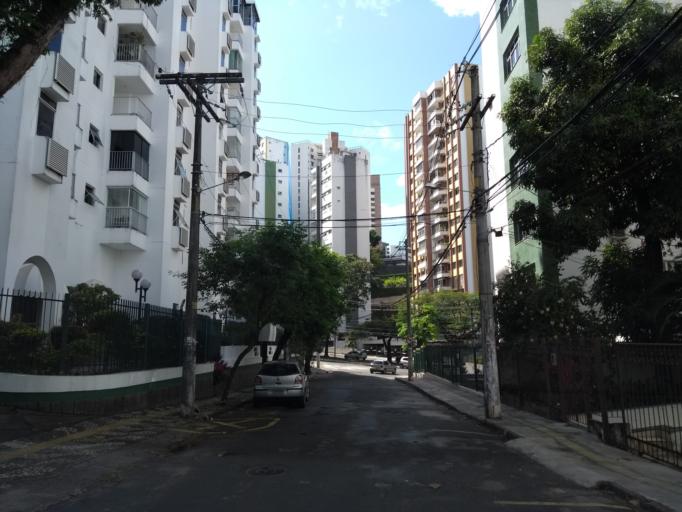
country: BR
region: Bahia
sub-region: Salvador
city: Salvador
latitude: -13.0046
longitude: -38.5213
